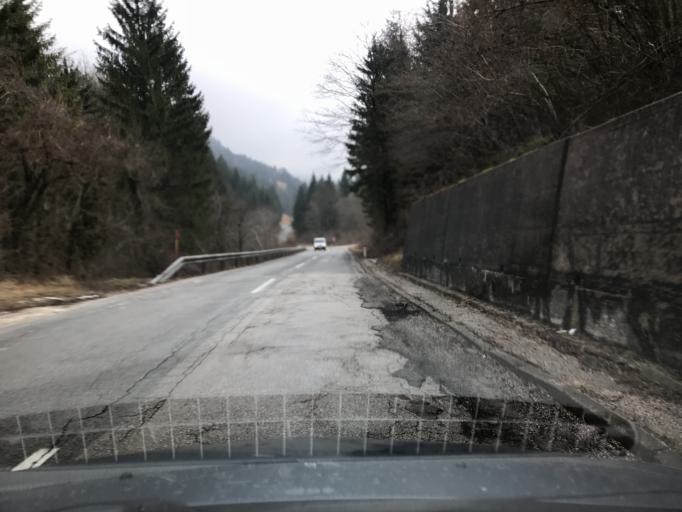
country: SI
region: Gornji Grad
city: Gornji Grad
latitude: 46.2142
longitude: 14.8136
